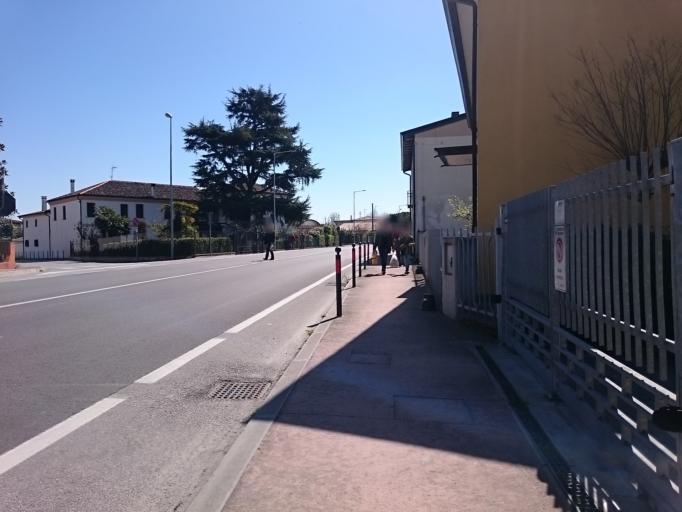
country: IT
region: Veneto
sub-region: Provincia di Padova
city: Brugine
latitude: 45.2960
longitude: 11.9954
